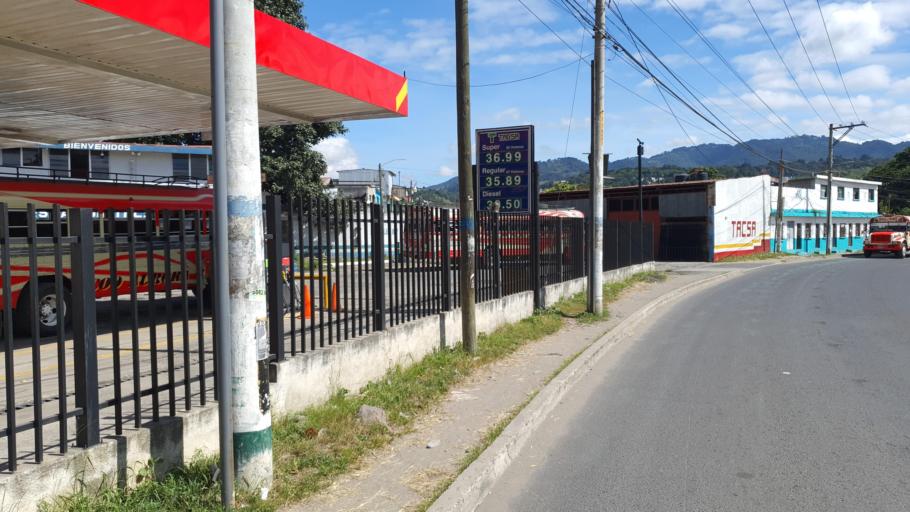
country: GT
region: Guatemala
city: Villa Canales
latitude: 14.4762
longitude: -90.5384
